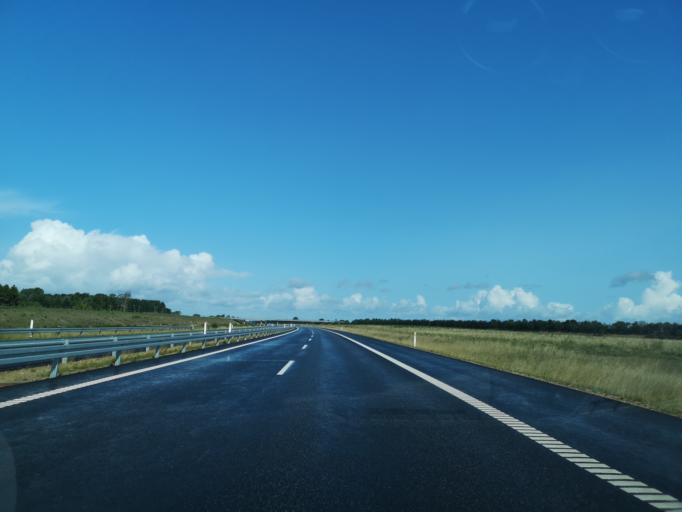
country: DK
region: Central Jutland
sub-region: Herning Kommune
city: Snejbjerg
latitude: 56.1927
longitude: 8.8869
